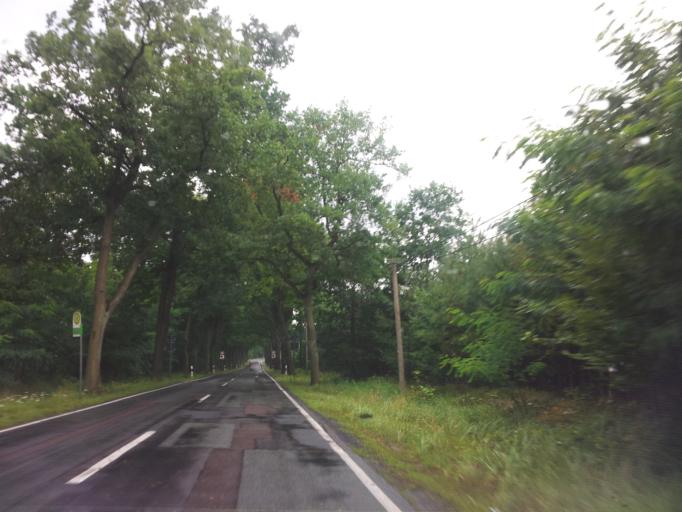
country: DE
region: Brandenburg
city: Graben
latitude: 52.2213
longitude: 12.4255
